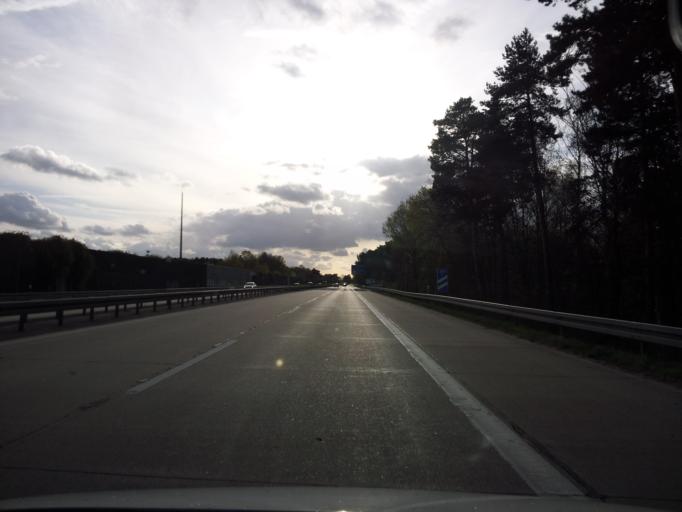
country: DE
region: Brandenburg
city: Cottbus
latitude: 51.7170
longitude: 14.3528
